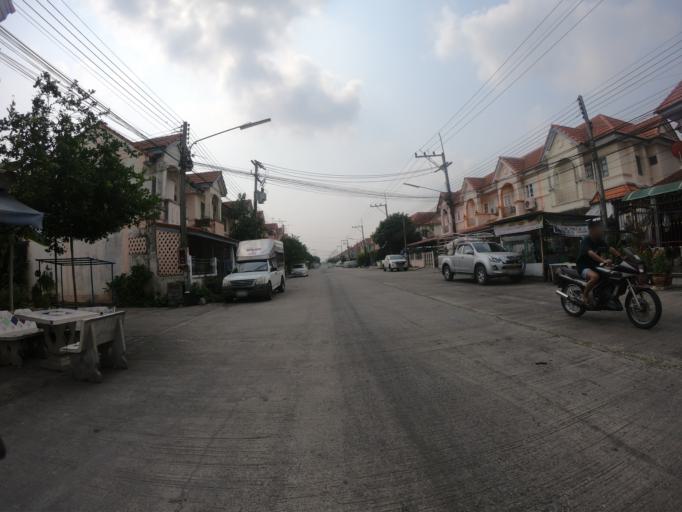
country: TH
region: Pathum Thani
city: Nong Suea
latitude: 14.0724
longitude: 100.8586
